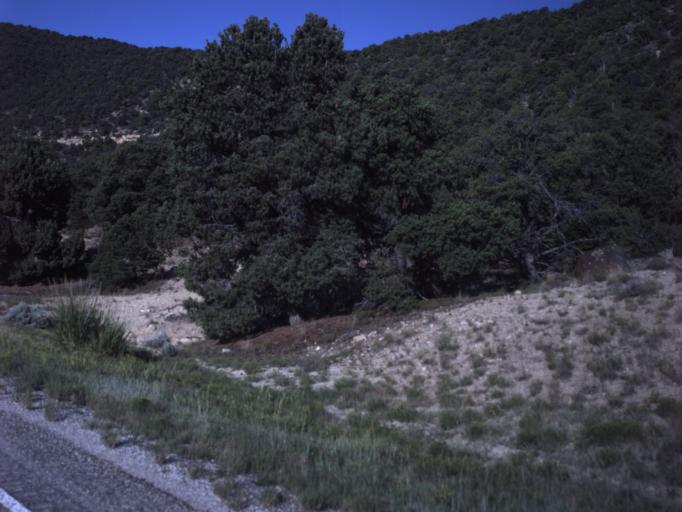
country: US
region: Utah
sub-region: Wayne County
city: Loa
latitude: 38.7464
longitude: -111.3929
